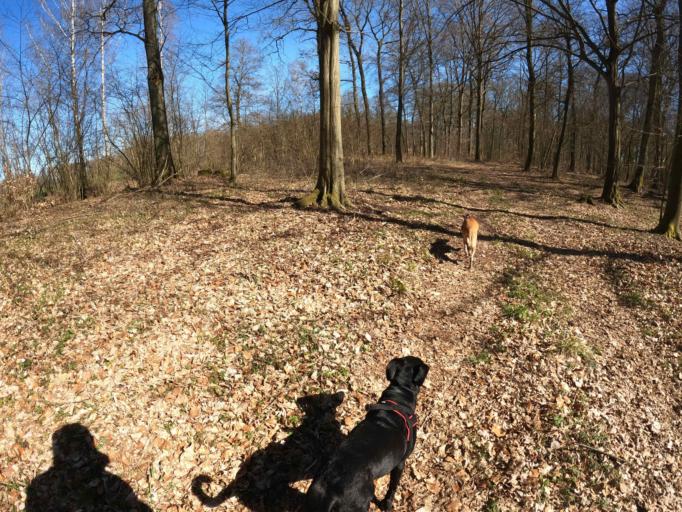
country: PL
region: West Pomeranian Voivodeship
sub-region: Powiat gryficki
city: Gryfice
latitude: 53.9295
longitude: 15.2814
